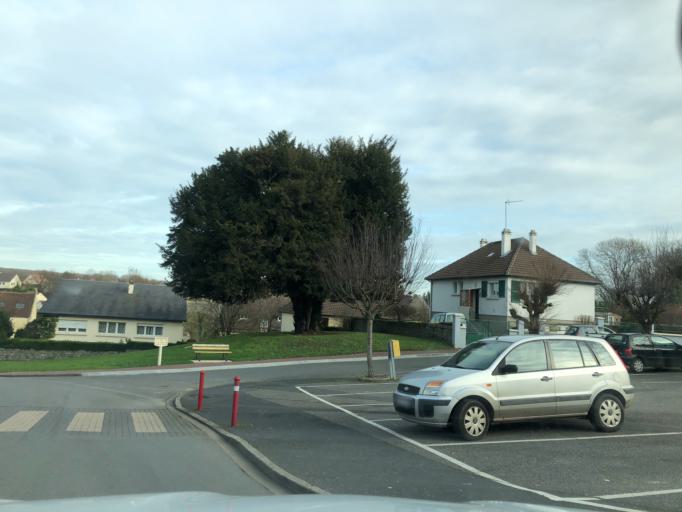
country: FR
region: Lower Normandy
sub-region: Departement du Calvados
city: Beuville
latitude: 49.2424
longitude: -0.3274
